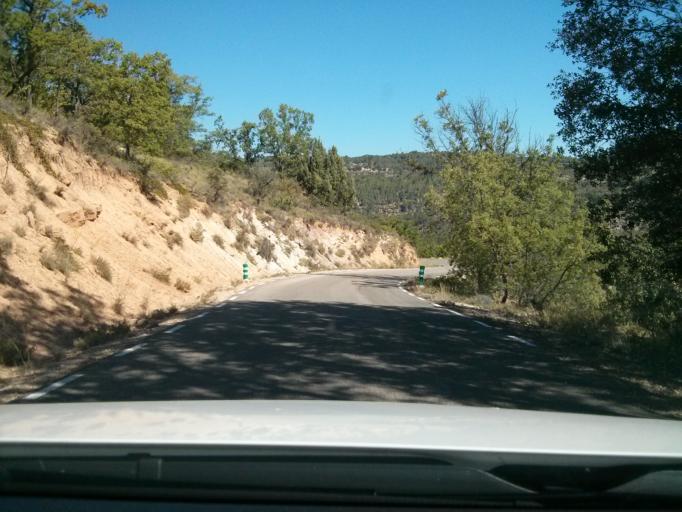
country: ES
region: Castille-La Mancha
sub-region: Provincia de Guadalajara
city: Mantiel
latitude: 40.6310
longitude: -2.6410
